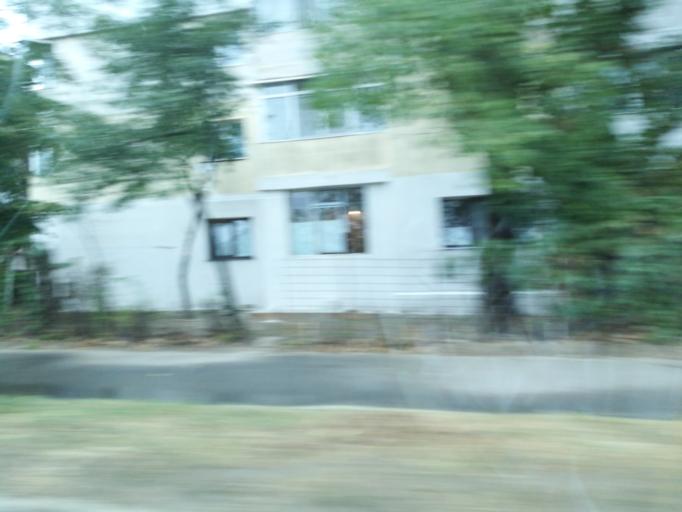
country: RO
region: Galati
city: Galati
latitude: 45.4563
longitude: 28.0163
